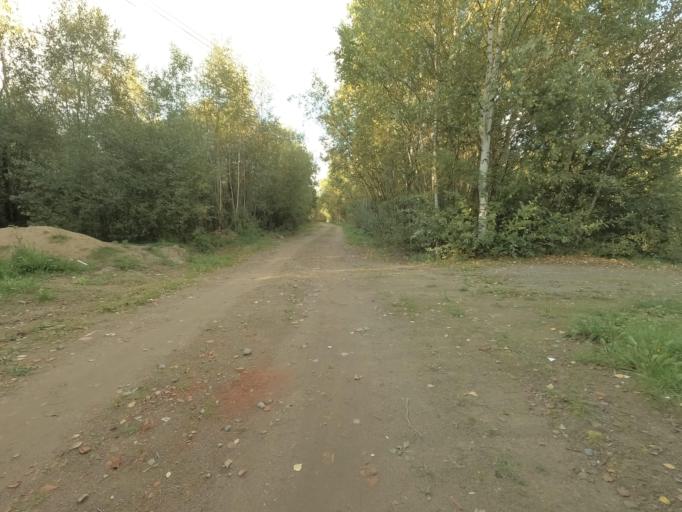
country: RU
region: Leningrad
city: Imeni Sverdlova
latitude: 59.8559
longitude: 30.7320
